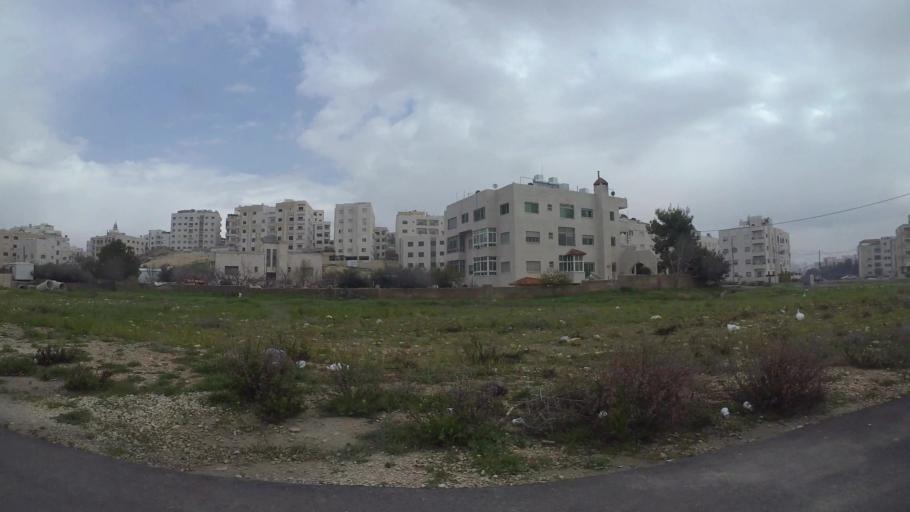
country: JO
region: Amman
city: Umm as Summaq
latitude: 31.9062
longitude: 35.8509
